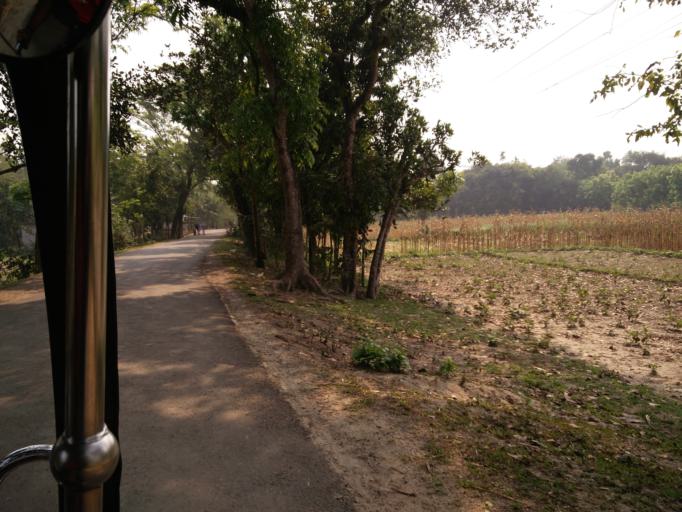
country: BD
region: Dhaka
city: Muktagacha
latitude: 24.9072
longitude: 90.2004
